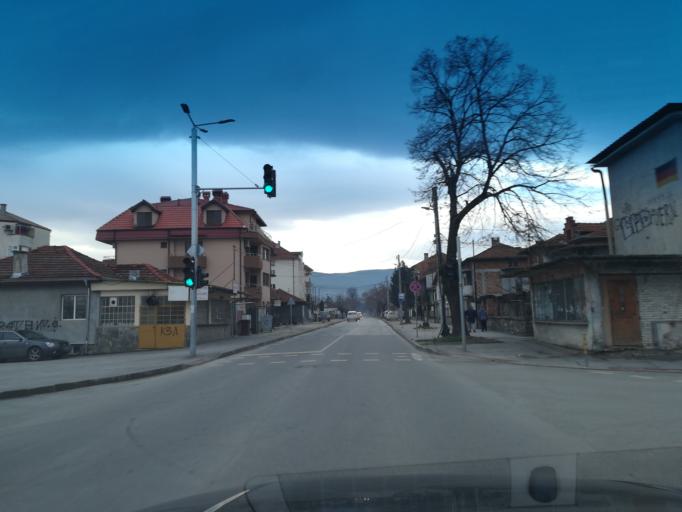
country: BG
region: Plovdiv
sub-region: Obshtina Plovdiv
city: Plovdiv
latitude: 42.1065
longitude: 24.7056
